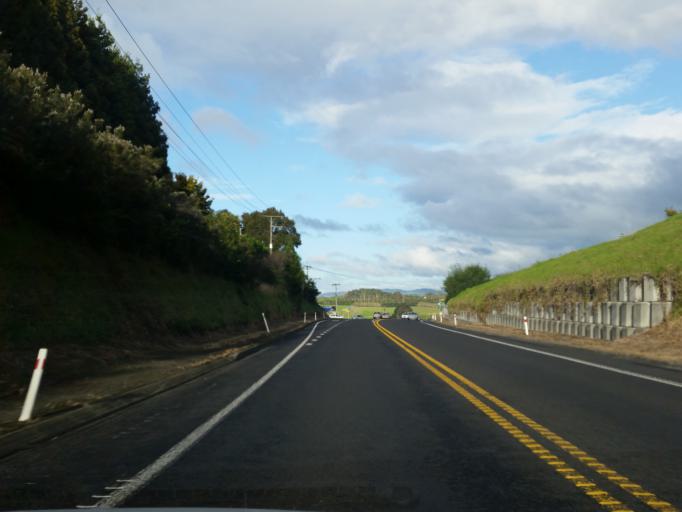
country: NZ
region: Bay of Plenty
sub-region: Western Bay of Plenty District
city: Katikati
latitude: -37.6641
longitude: 176.0134
